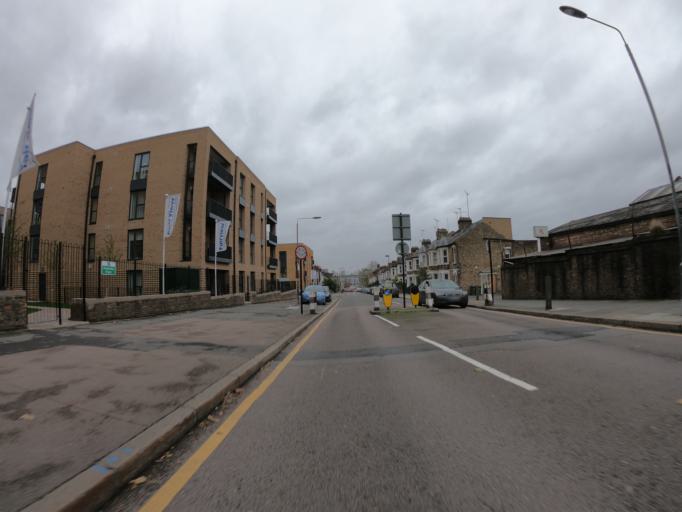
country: GB
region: England
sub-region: Greater London
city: Blackheath
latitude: 51.4857
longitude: 0.0255
